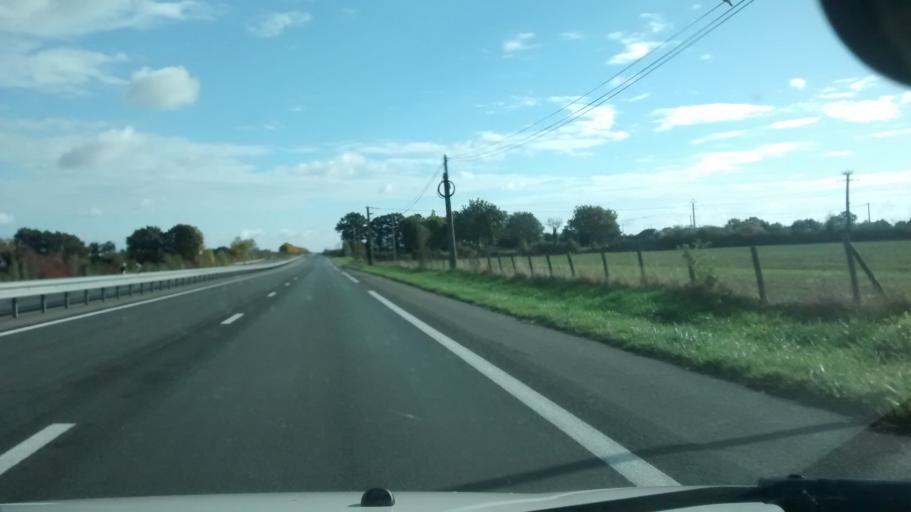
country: FR
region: Pays de la Loire
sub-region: Departement de Maine-et-Loire
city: Pouance
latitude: 47.7353
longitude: -1.1423
